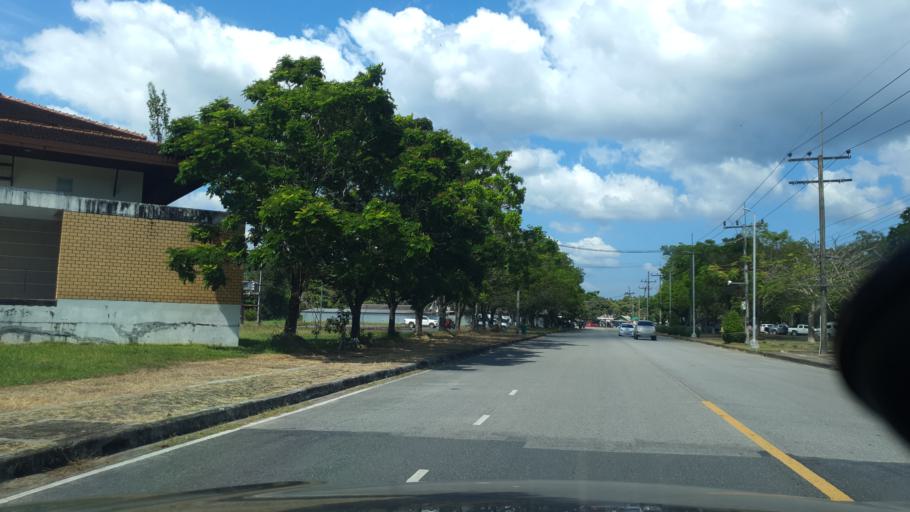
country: TH
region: Phangnga
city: Phang Nga
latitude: 8.4016
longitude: 98.5123
